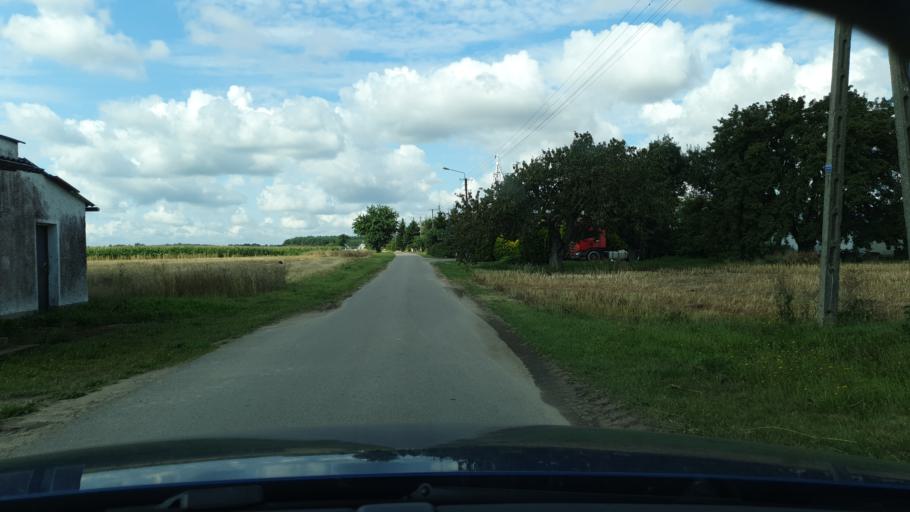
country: PL
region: Pomeranian Voivodeship
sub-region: Powiat czluchowski
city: Przechlewo
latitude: 53.8089
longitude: 17.3817
